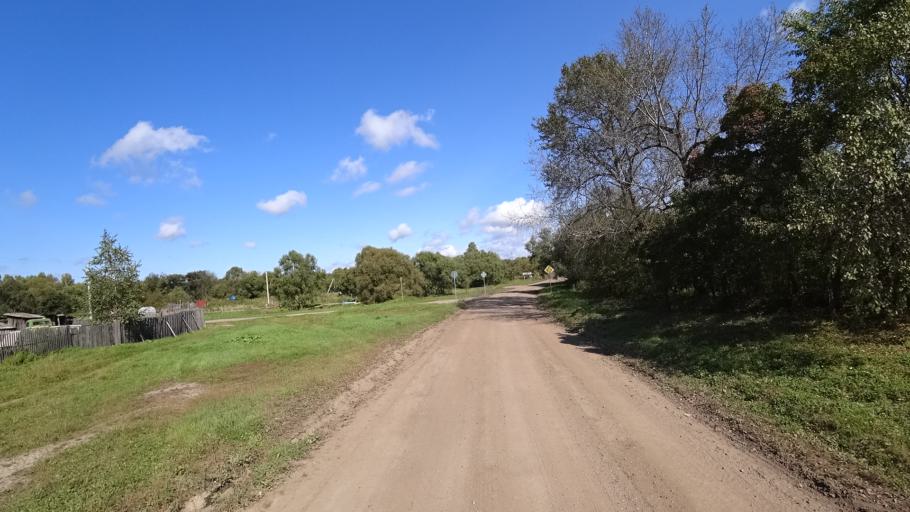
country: RU
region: Amur
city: Arkhara
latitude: 49.4057
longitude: 130.1568
